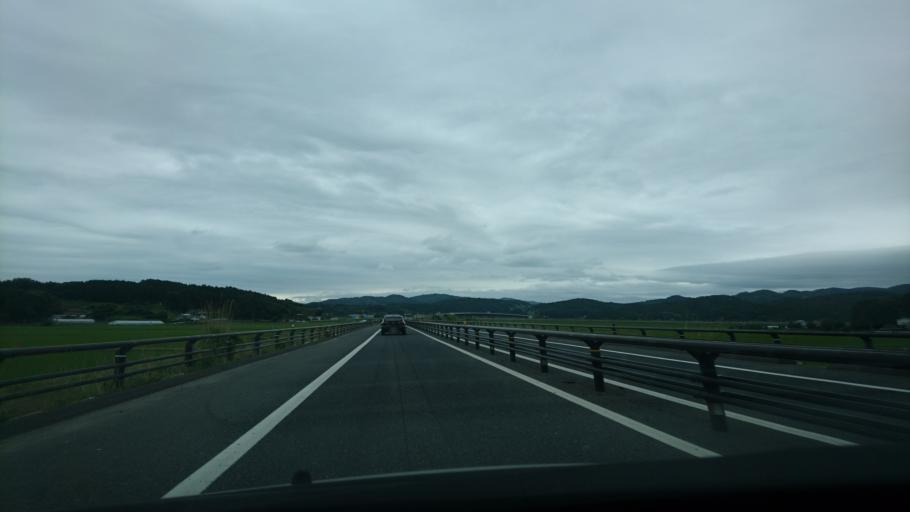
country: JP
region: Miyagi
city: Wakuya
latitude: 38.6919
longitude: 141.2775
